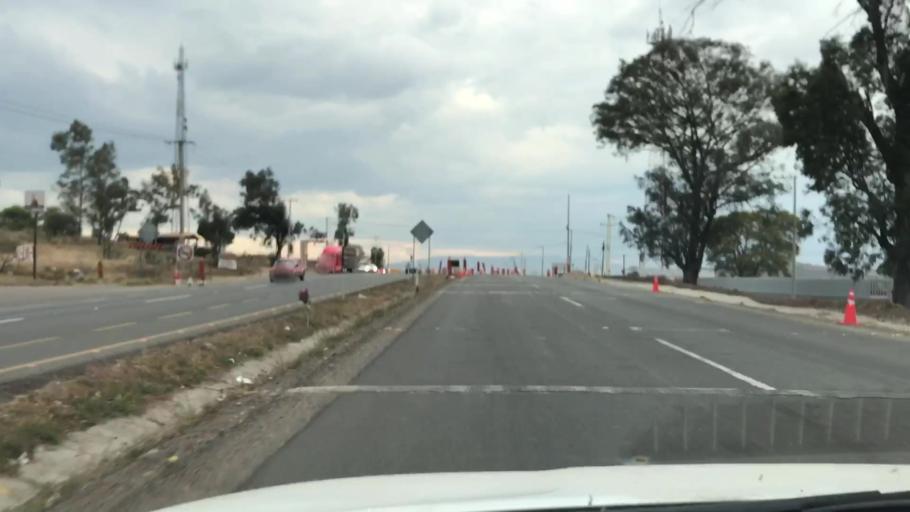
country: MX
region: Guanajuato
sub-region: Irapuato
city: San Ignacio de Rivera (Ojo de Agua)
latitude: 20.5650
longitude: -101.4475
